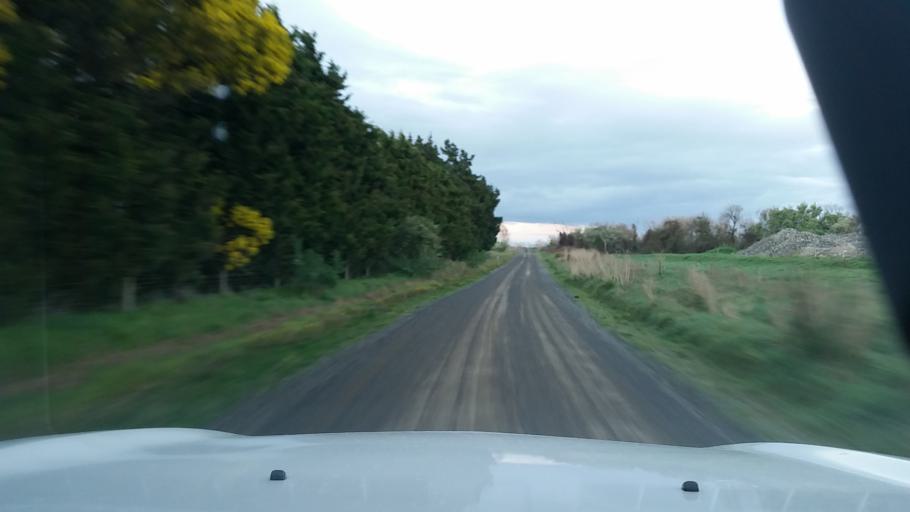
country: NZ
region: Wellington
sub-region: South Wairarapa District
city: Waipawa
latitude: -41.1648
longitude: 175.3545
